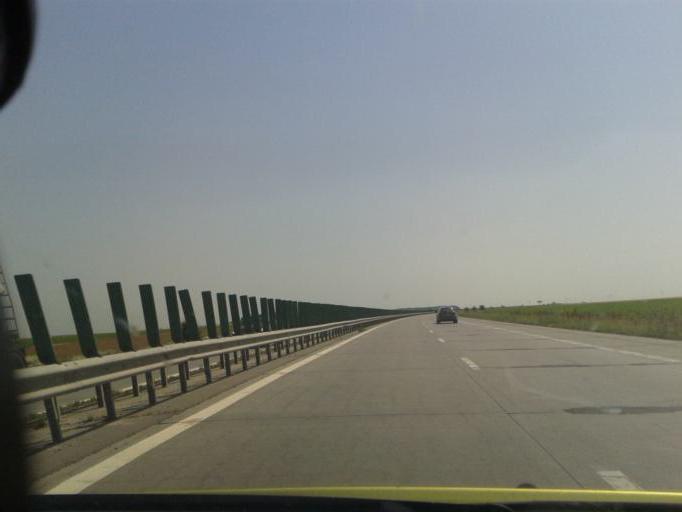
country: RO
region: Ilfov
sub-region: Comuna Branesti
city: Islaz
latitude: 44.4377
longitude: 26.3802
